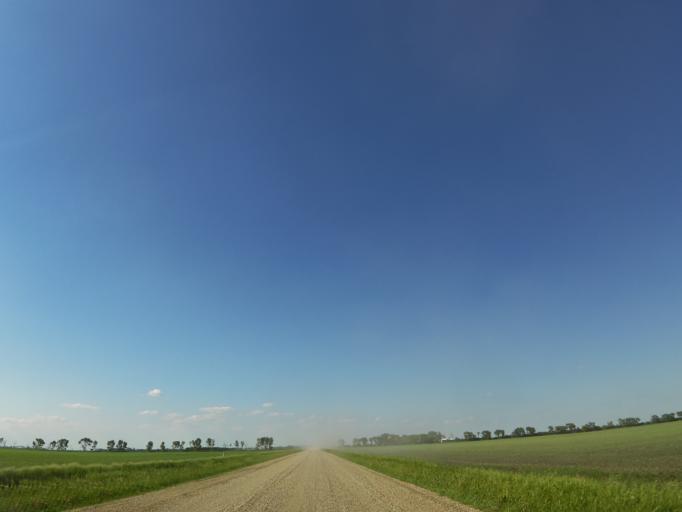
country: US
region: North Dakota
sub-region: Walsh County
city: Grafton
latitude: 48.3249
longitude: -97.2554
